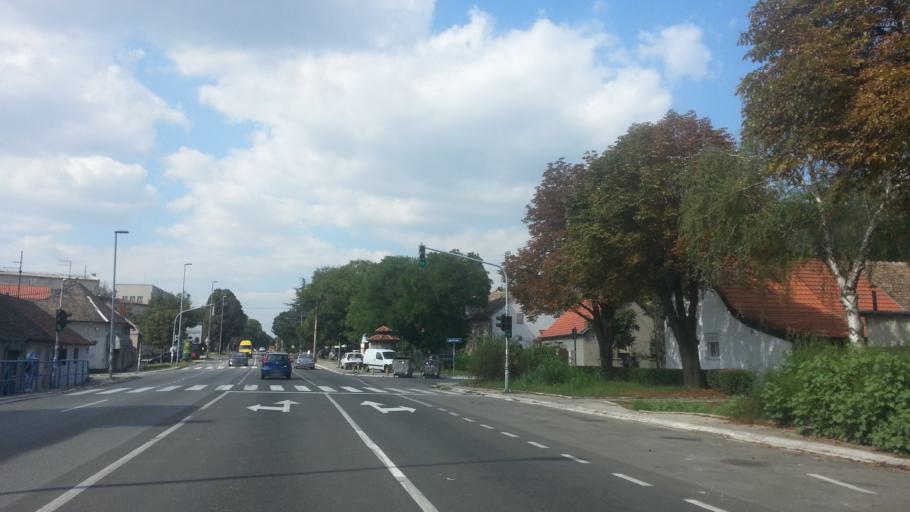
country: RS
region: Central Serbia
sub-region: Belgrade
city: Zemun
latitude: 44.8532
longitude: 20.3918
